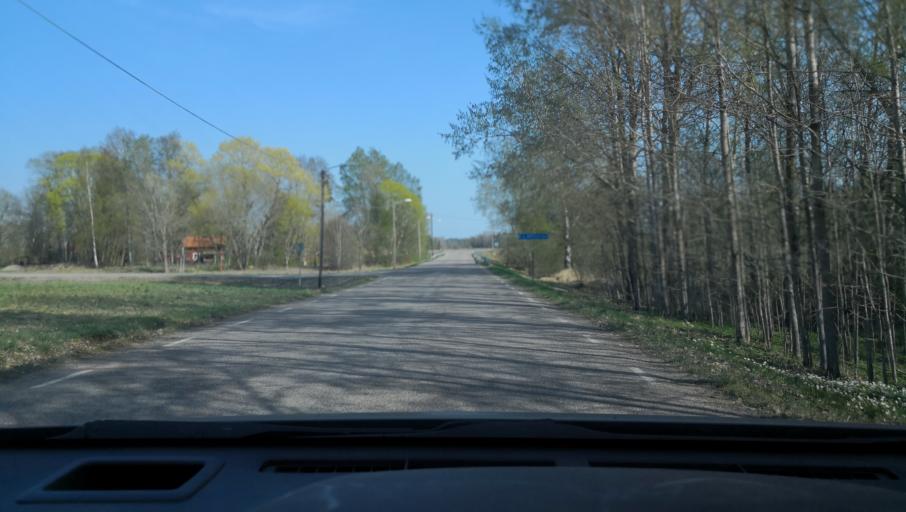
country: SE
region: Uppsala
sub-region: Heby Kommun
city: Heby
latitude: 60.0343
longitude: 16.7977
